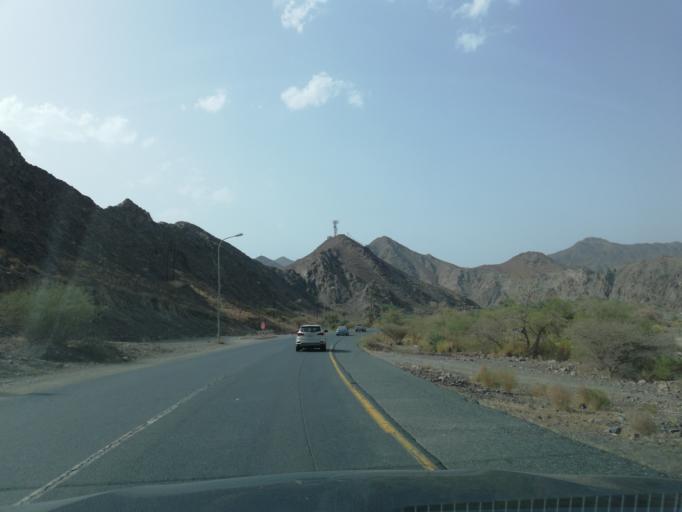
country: OM
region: Muhafazat ad Dakhiliyah
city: Sufalat Sama'il
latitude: 23.2299
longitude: 58.0777
